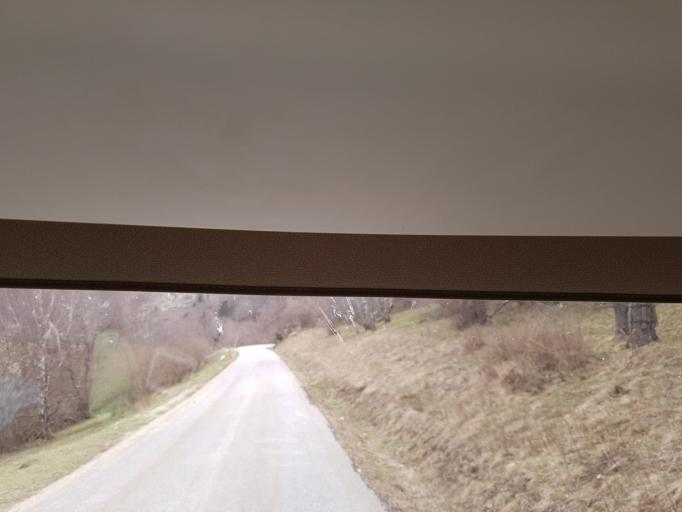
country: FR
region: Languedoc-Roussillon
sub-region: Departement de l'Aude
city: Quillan
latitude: 42.6632
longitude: 2.1275
